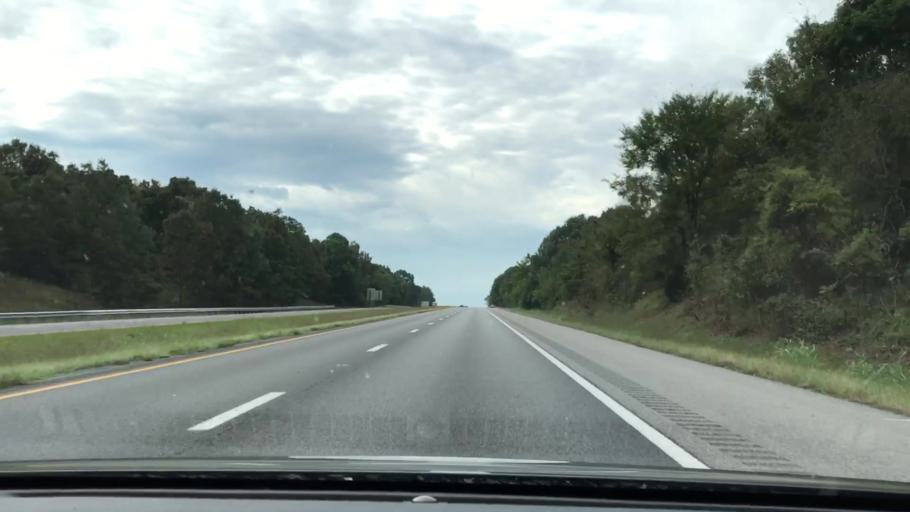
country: US
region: Kentucky
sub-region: Marshall County
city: Benton
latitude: 36.9133
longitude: -88.3502
